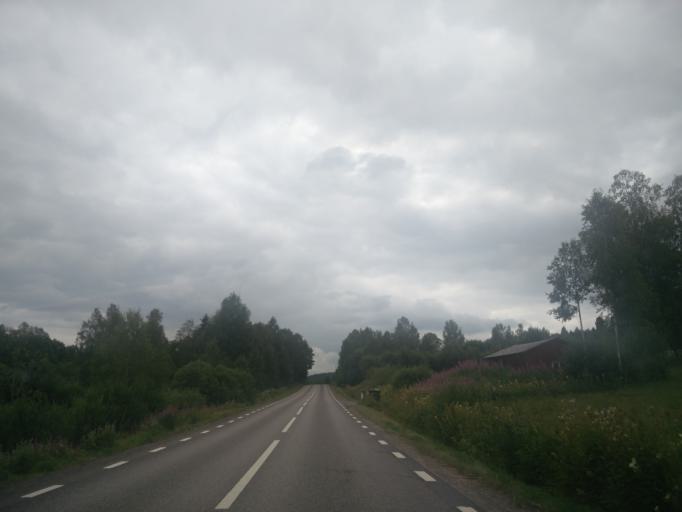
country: SE
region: Vaermland
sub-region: Torsby Kommun
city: Torsby
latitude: 59.9357
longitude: 12.9005
